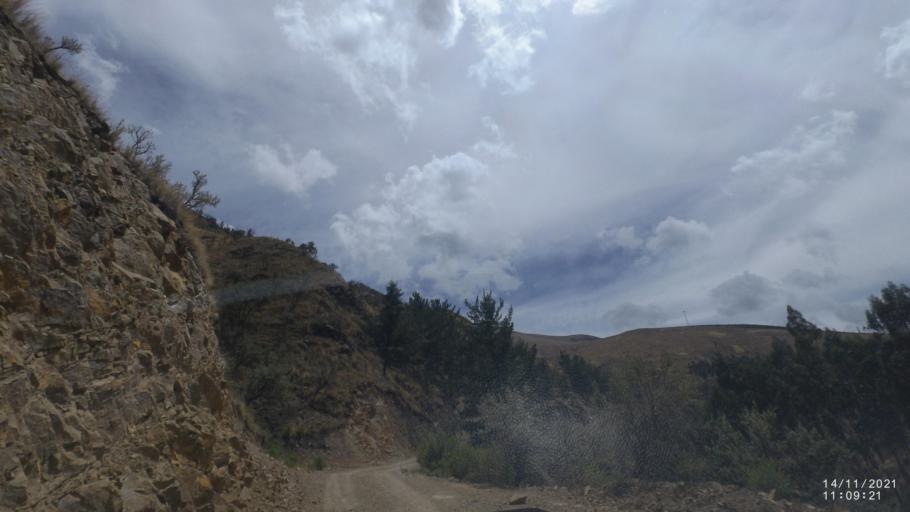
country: BO
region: Cochabamba
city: Cochabamba
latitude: -17.3310
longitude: -66.0537
